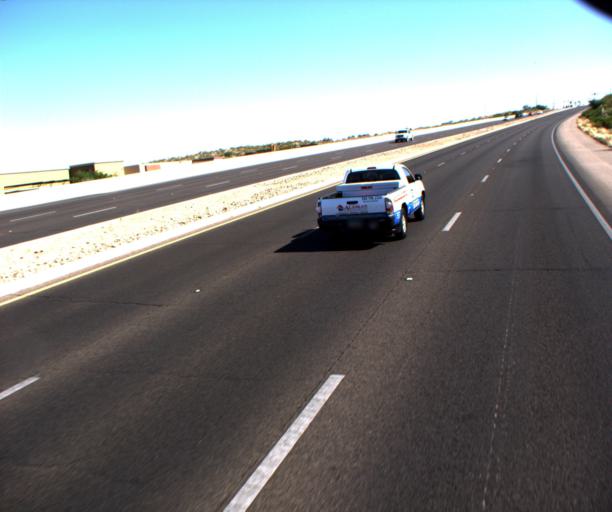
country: US
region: Arizona
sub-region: Pima County
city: Oro Valley
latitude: 32.4214
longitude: -110.9368
